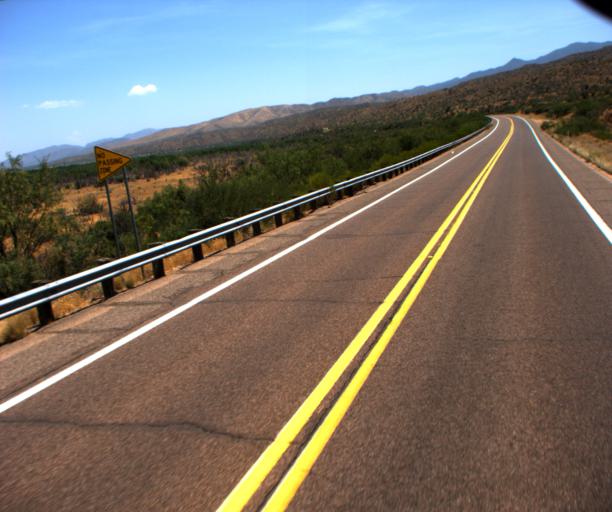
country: US
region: Arizona
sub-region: Gila County
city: Tonto Basin
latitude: 33.7840
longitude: -111.2636
